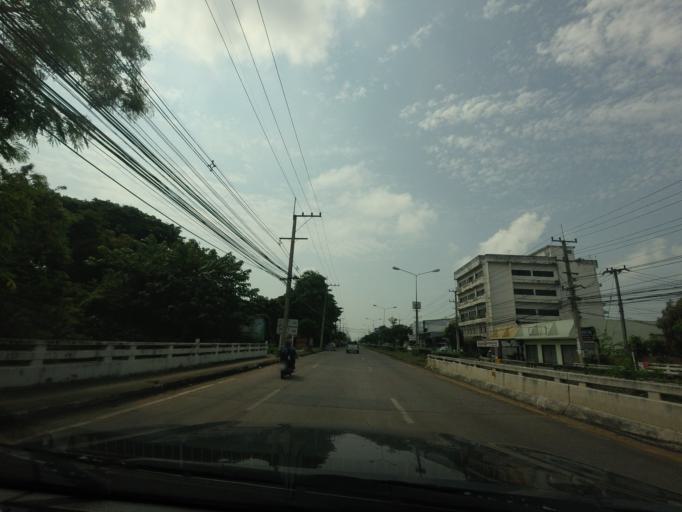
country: TH
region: Phrae
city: Phrae
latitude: 18.1238
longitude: 100.1418
